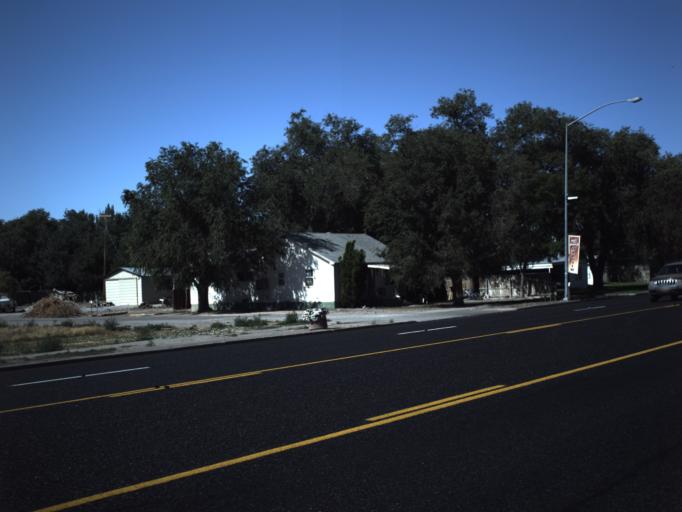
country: US
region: Utah
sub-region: Millard County
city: Delta
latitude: 39.3524
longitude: -112.5687
